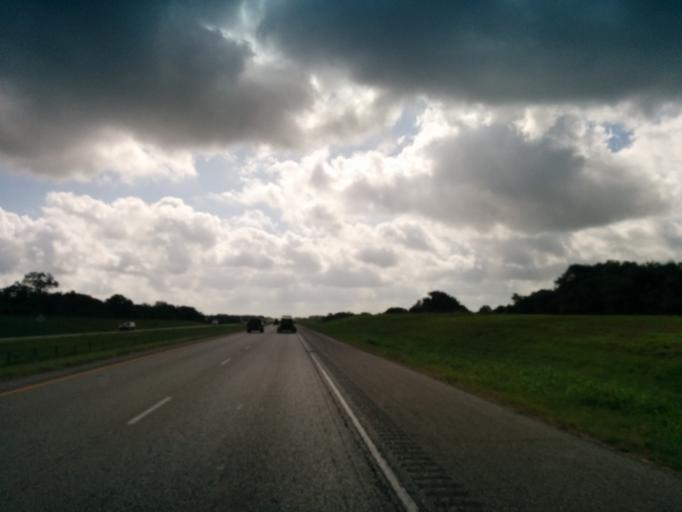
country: US
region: Texas
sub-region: Gonzales County
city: Waelder
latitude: 29.6629
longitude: -97.3772
